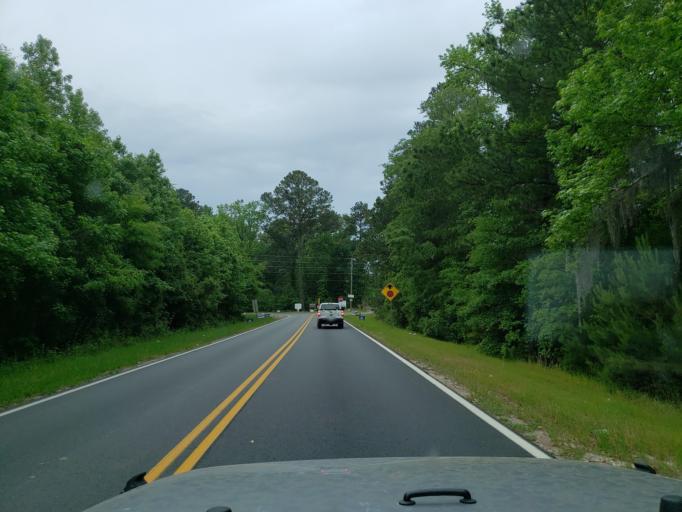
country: US
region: Georgia
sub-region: Chatham County
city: Port Wentworth
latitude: 32.1809
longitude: -81.1949
